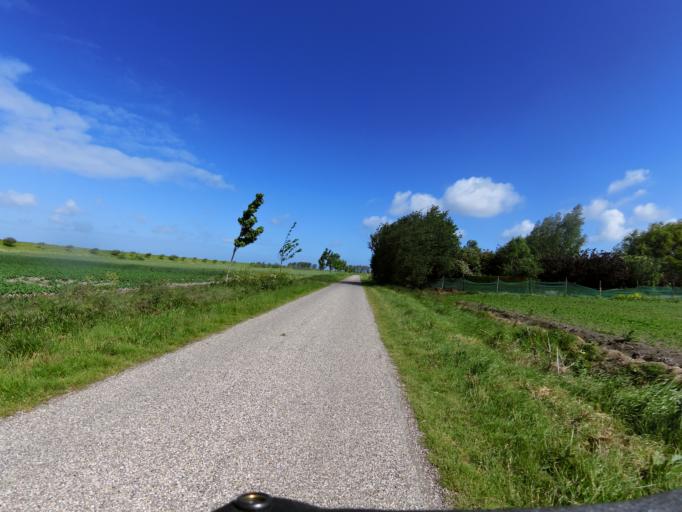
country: NL
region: Zeeland
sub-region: Schouwen-Duiveland
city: Scharendijke
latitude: 51.6863
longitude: 3.9269
